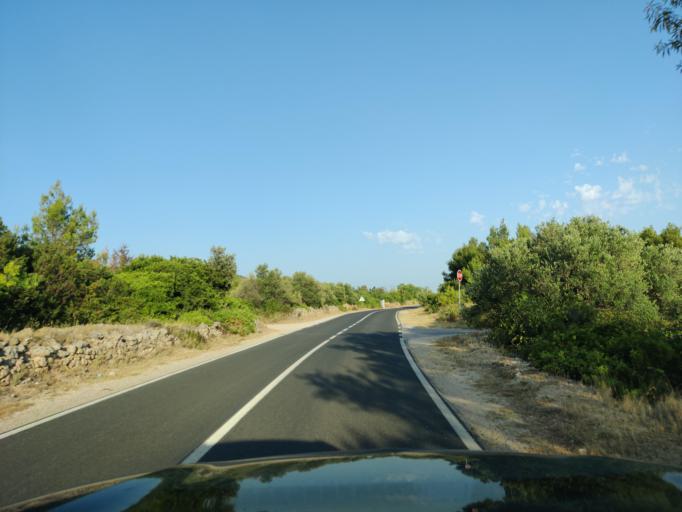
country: HR
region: Sibensko-Kniniska
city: Tribunj
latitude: 43.7659
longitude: 15.7348
